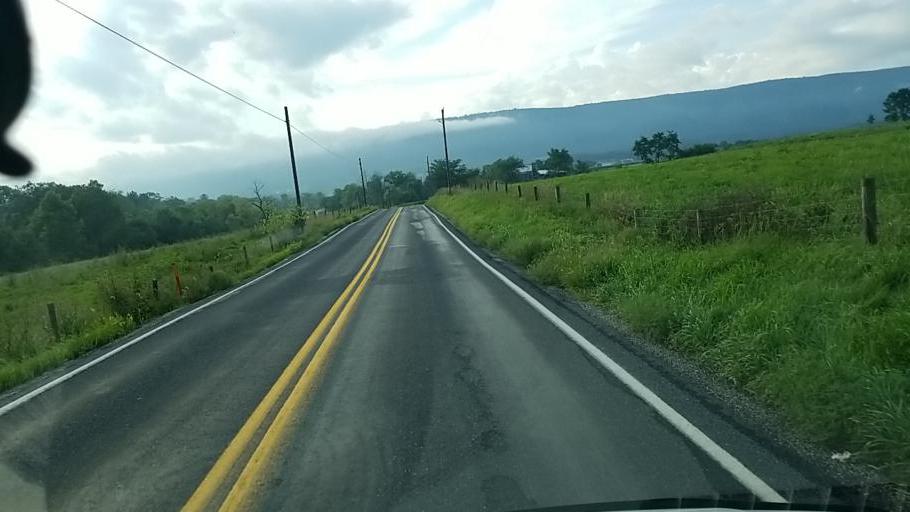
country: US
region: Pennsylvania
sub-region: Cumberland County
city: Newville
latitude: 40.1939
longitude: -77.4944
